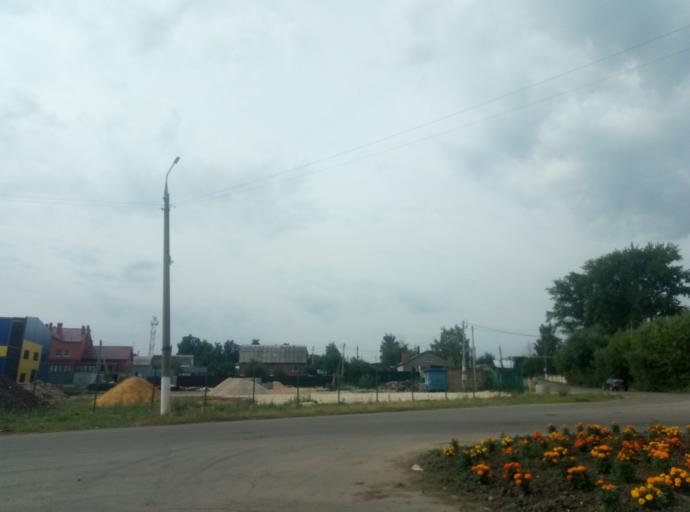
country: RU
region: Tula
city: Bogoroditsk
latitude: 53.7845
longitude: 38.1186
